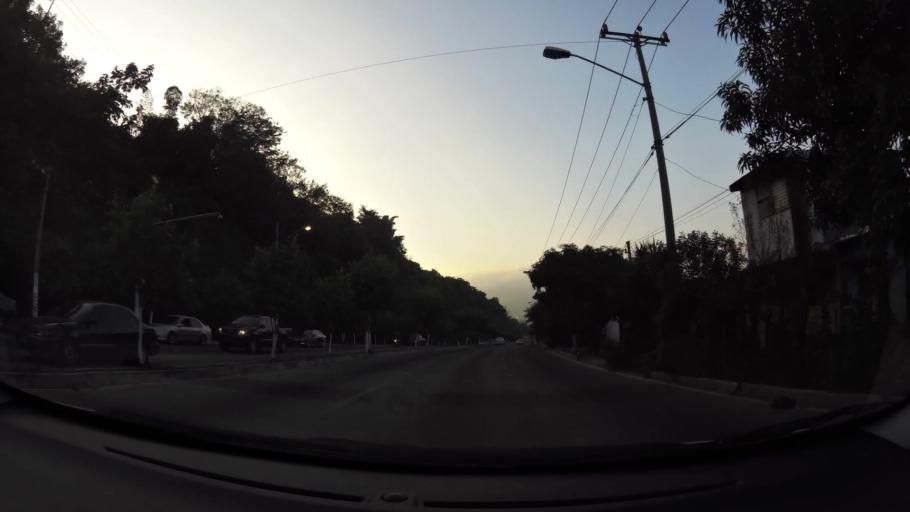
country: SV
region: San Salvador
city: San Salvador
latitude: 13.6794
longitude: -89.2127
